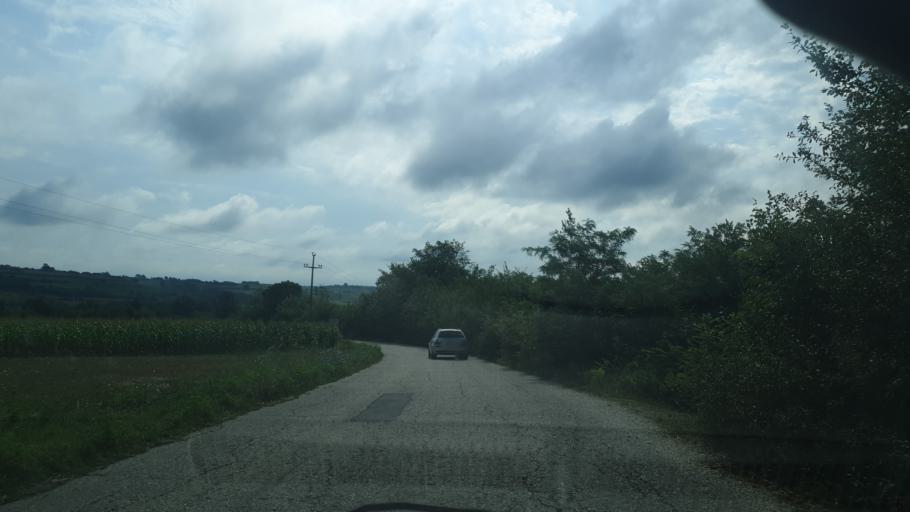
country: RS
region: Central Serbia
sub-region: Sumadijski Okrug
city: Kragujevac
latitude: 44.0959
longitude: 20.7880
